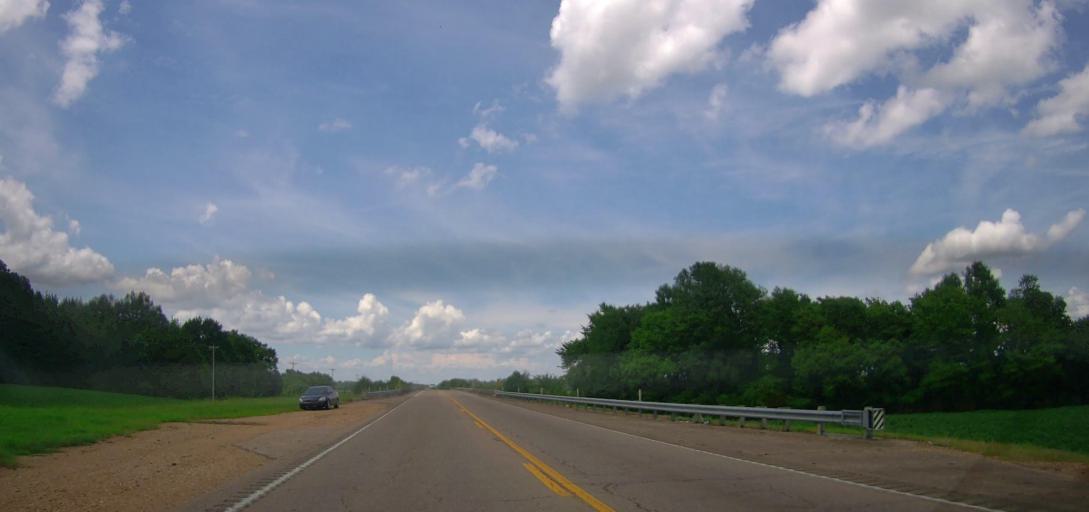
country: US
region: Mississippi
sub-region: Lee County
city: Shannon
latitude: 34.1361
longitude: -88.7194
